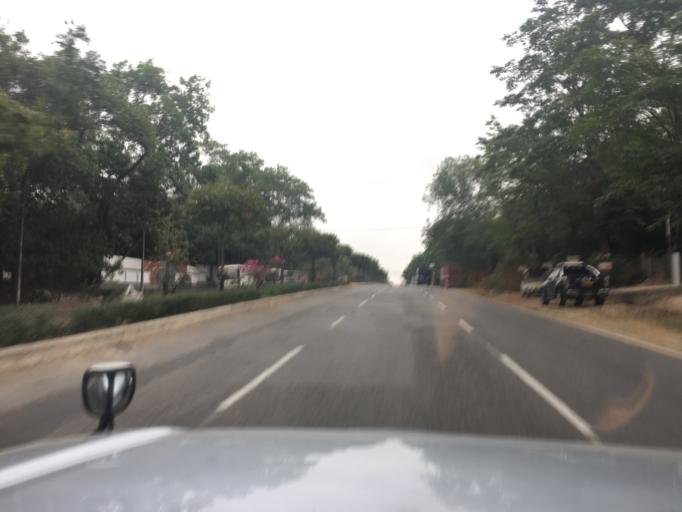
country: MM
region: Bago
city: Bago
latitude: 17.2374
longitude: 96.4626
